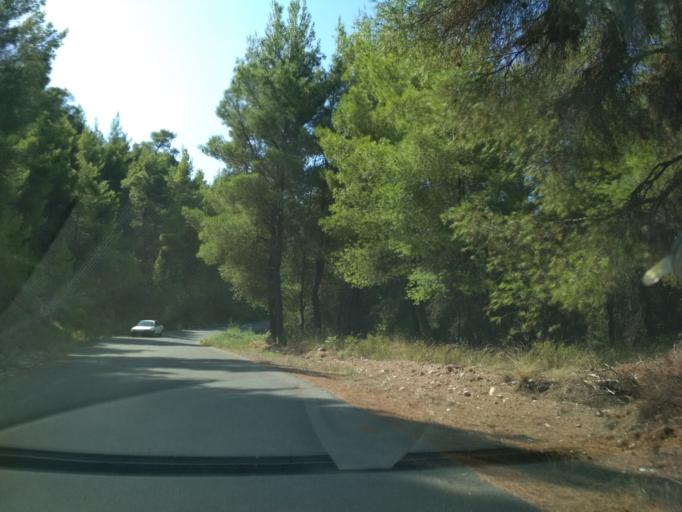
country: GR
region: Central Greece
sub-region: Nomos Evvoias
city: Roviai
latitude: 38.8232
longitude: 23.2667
